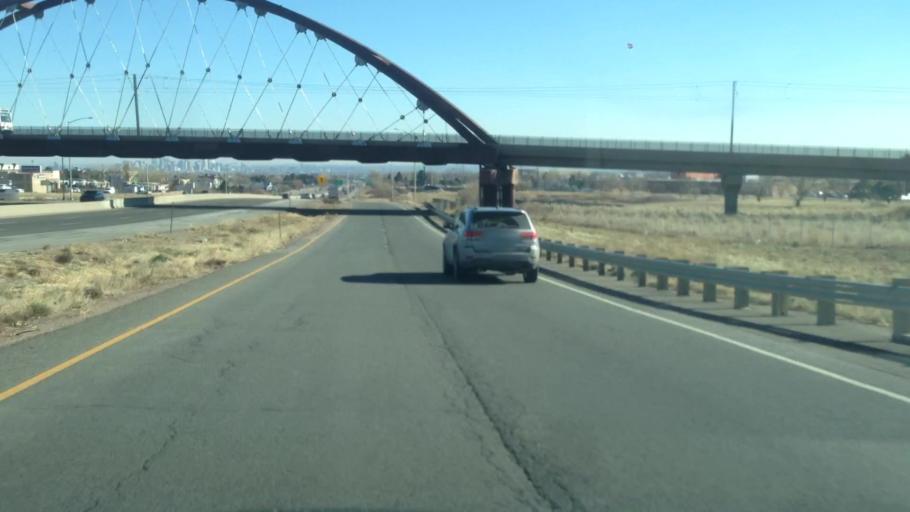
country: US
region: Colorado
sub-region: Jefferson County
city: Applewood
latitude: 39.7251
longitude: -105.1264
